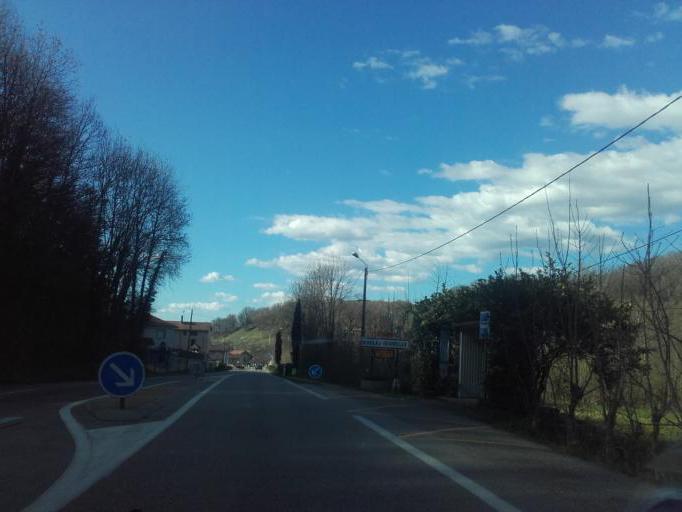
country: FR
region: Rhone-Alpes
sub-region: Departement de l'Isere
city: Nivolas-Vermelle
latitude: 45.5468
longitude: 5.3101
